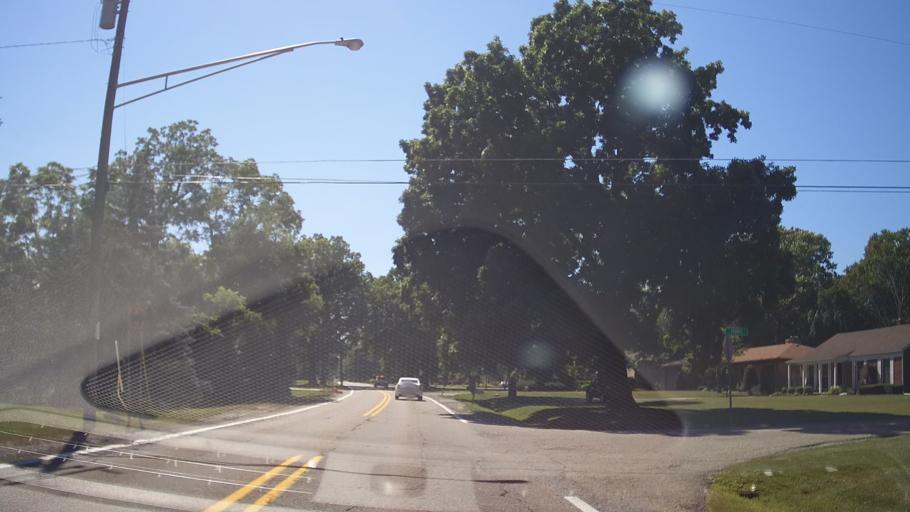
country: US
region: Michigan
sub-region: Macomb County
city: Clinton
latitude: 42.5883
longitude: -82.9071
